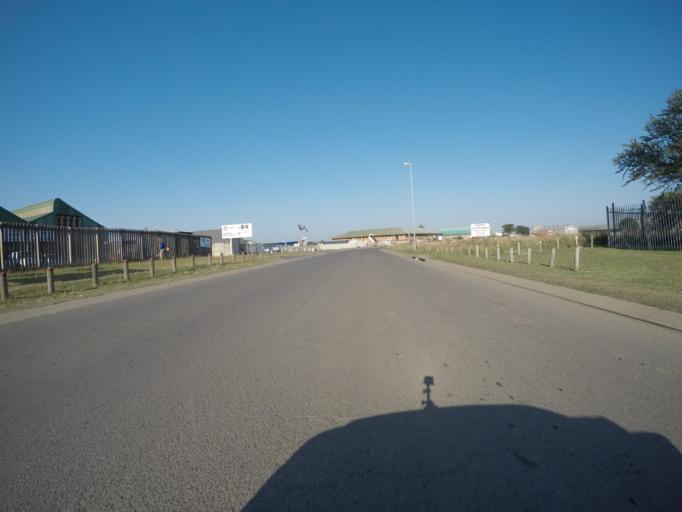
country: ZA
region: KwaZulu-Natal
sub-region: uThungulu District Municipality
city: Richards Bay
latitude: -28.7506
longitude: 32.0290
